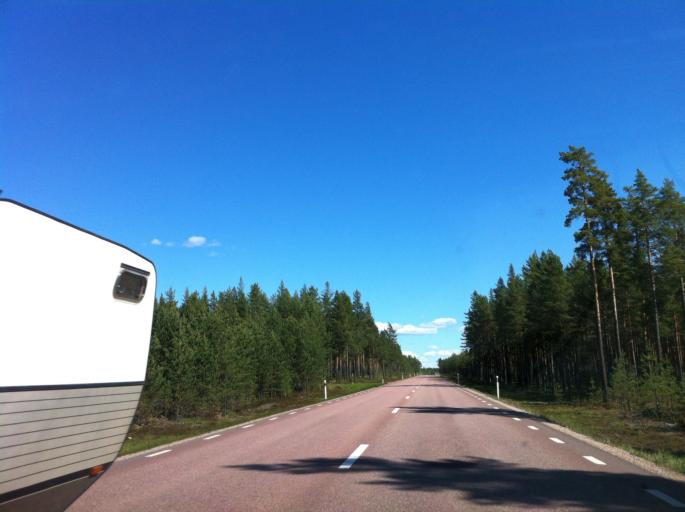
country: SE
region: Dalarna
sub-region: Leksand Municipality
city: Siljansnas
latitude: 60.9467
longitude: 14.7415
